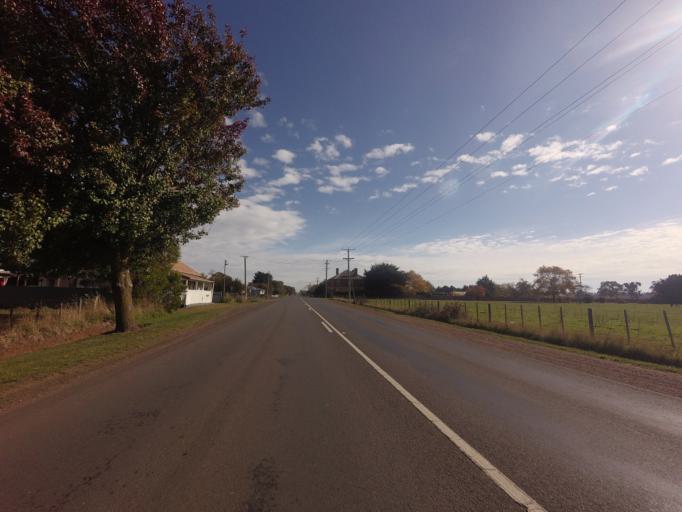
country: AU
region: Tasmania
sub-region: Meander Valley
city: Westbury
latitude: -41.5260
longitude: 146.8521
